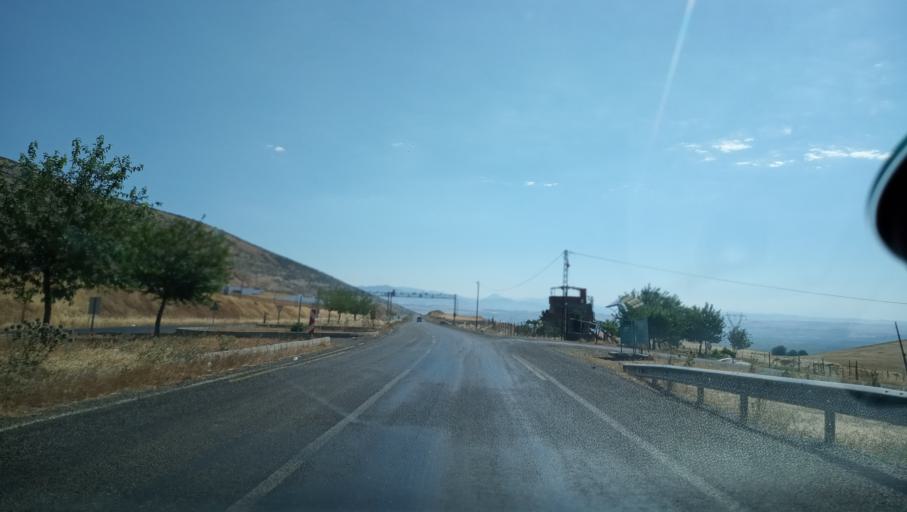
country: TR
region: Diyarbakir
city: Malabadi
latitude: 38.1193
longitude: 41.1465
